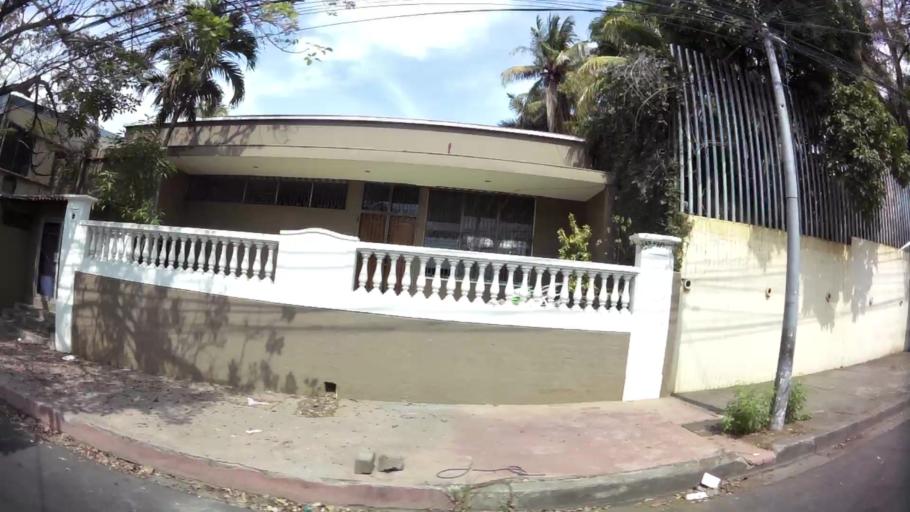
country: NI
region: Managua
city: Managua
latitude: 12.1416
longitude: -86.2762
